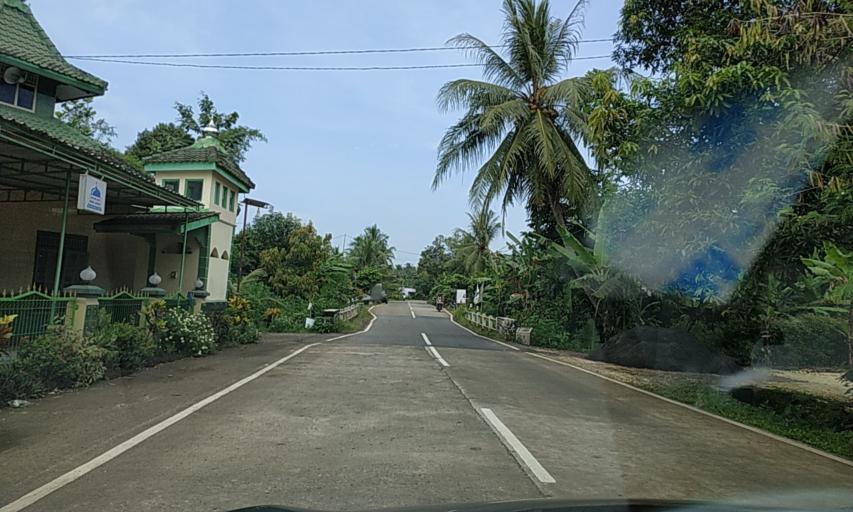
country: ID
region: Central Java
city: Tambangan
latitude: -7.4820
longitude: 108.8368
